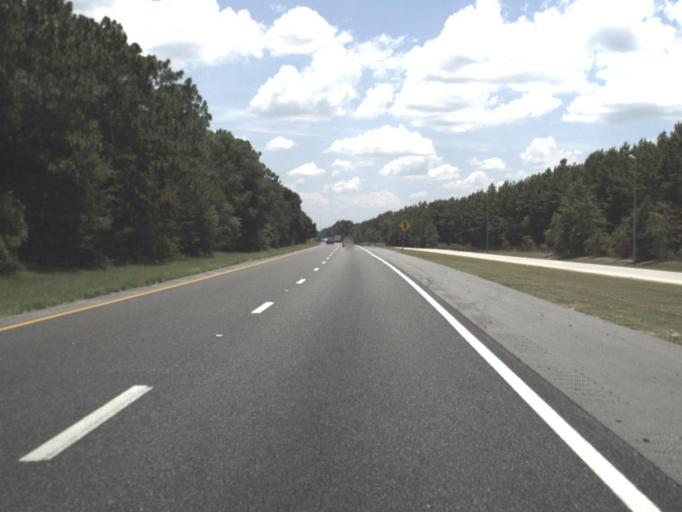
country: US
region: Florida
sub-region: Madison County
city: Madison
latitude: 30.3727
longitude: -83.2673
